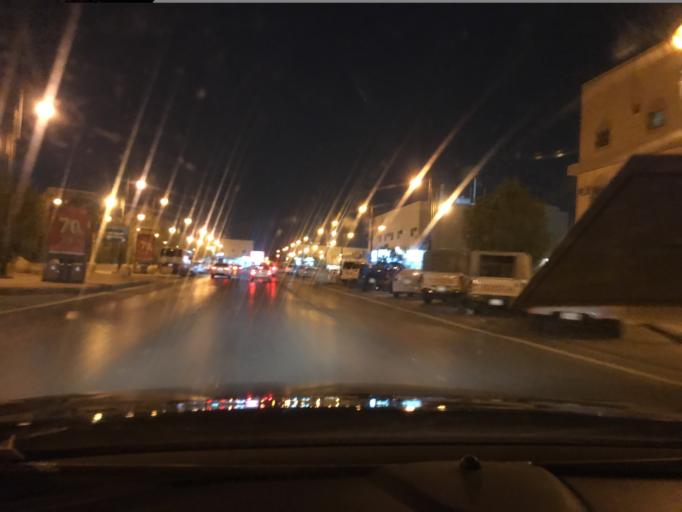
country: SA
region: Ar Riyad
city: Riyadh
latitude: 24.7417
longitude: 46.7666
